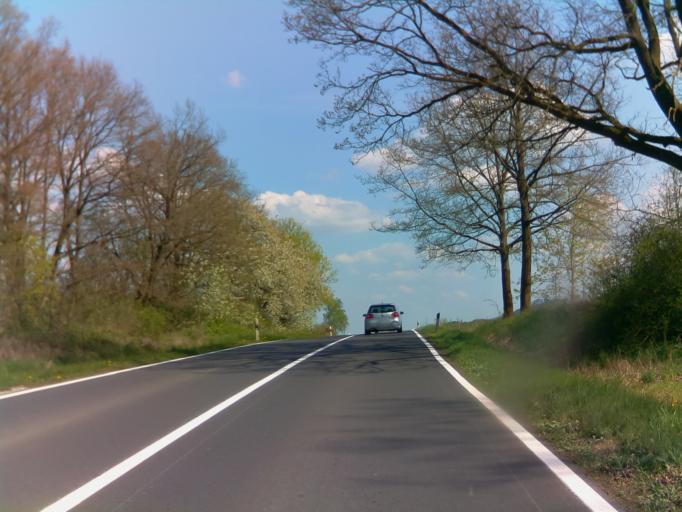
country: DE
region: Thuringia
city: Westhausen
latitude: 50.3679
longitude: 10.6621
